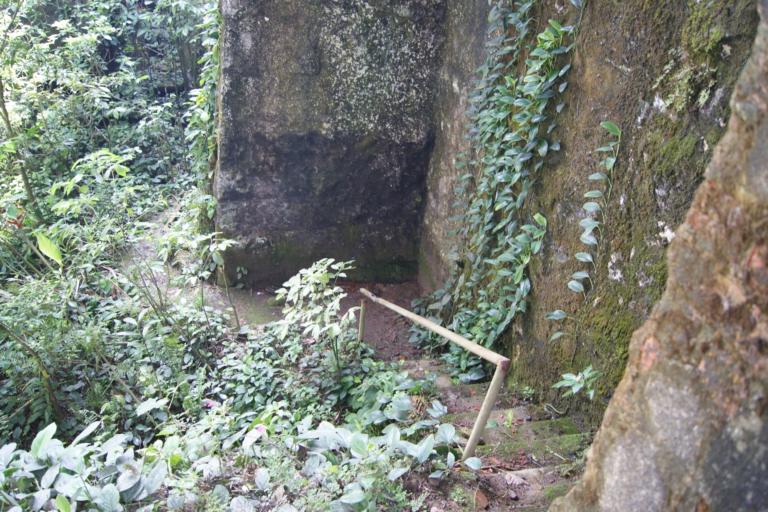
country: BR
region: Sao Paulo
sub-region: Rio Grande Da Serra
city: Rio Grande da Serra
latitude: -23.8077
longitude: -46.3311
